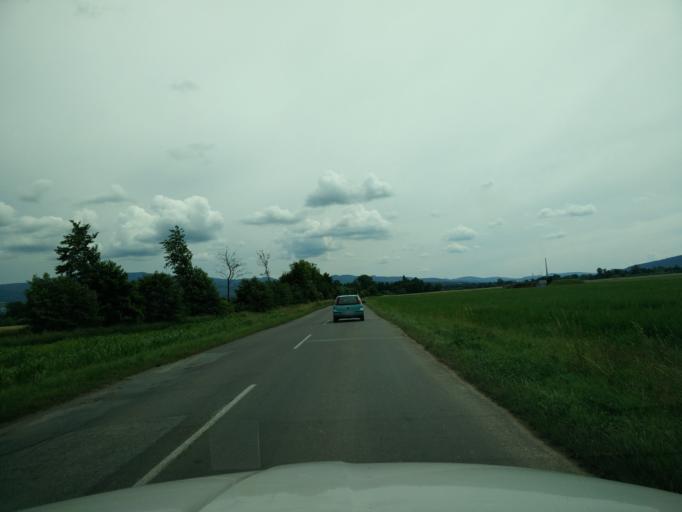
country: SK
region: Nitriansky
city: Bojnice
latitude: 48.7551
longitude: 18.5716
